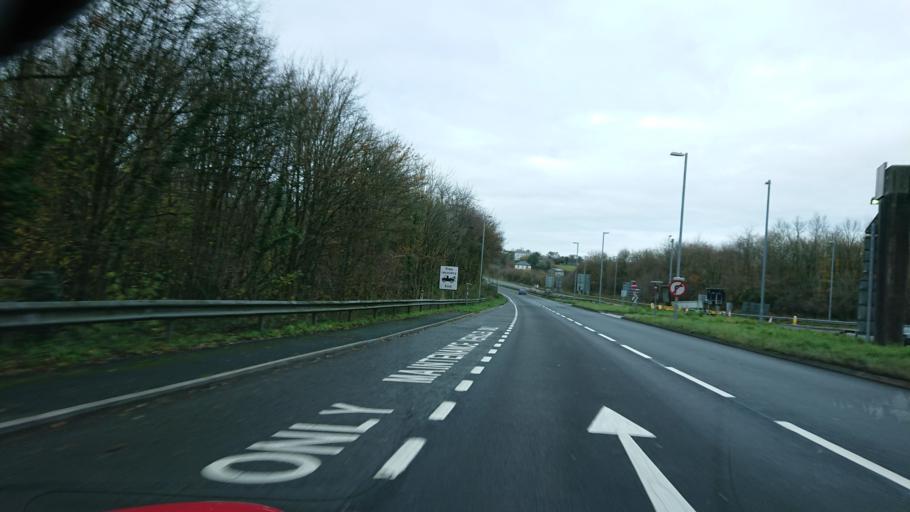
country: GB
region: England
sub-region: Cornwall
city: Saltash
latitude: 50.4134
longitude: -4.2166
